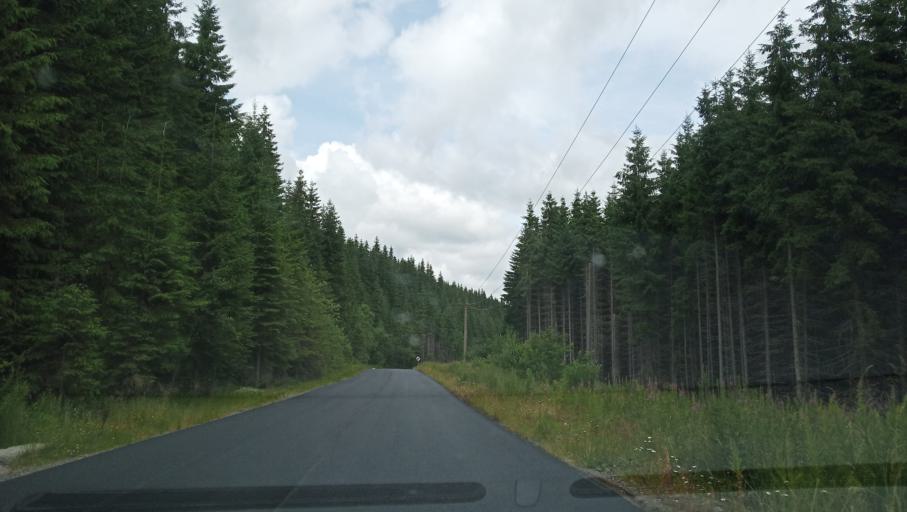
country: RO
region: Gorj
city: Novaci-Straini
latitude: 45.4238
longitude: 23.6931
